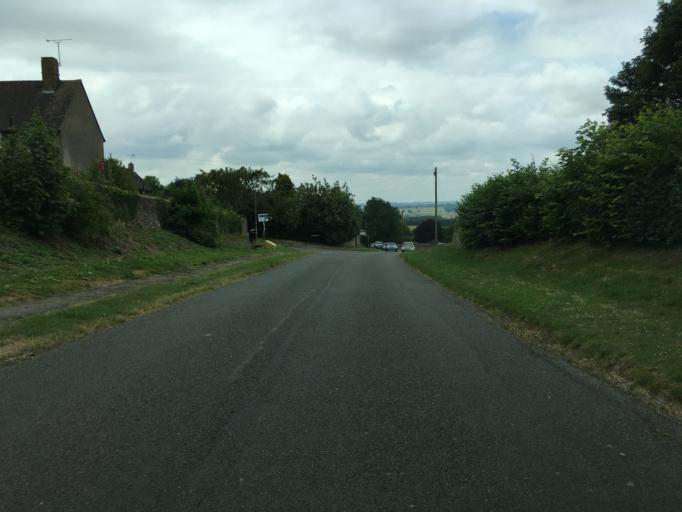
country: GB
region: England
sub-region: Oxfordshire
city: Somerton
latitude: 51.9972
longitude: -1.2527
